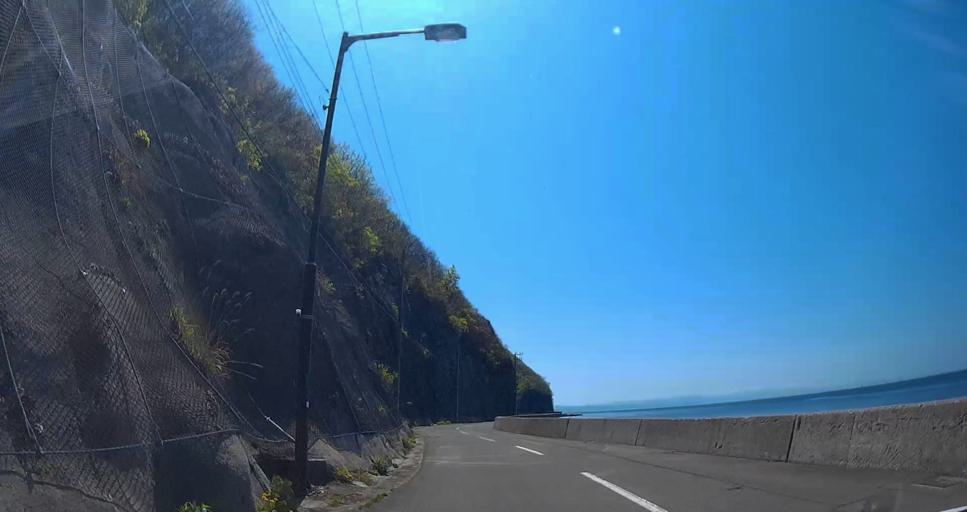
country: JP
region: Aomori
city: Aomori Shi
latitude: 41.1397
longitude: 140.7747
